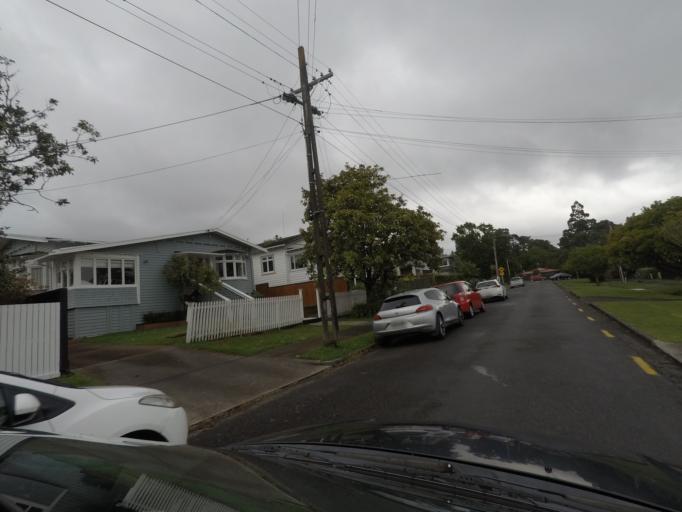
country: NZ
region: Auckland
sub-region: Auckland
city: Auckland
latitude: -36.8930
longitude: 174.7299
